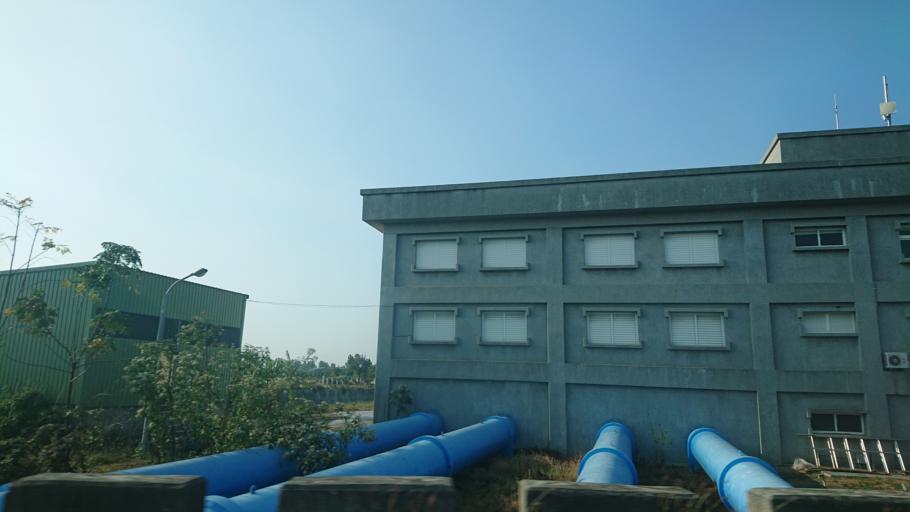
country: TW
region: Taiwan
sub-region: Tainan
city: Tainan
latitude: 23.1355
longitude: 120.2383
